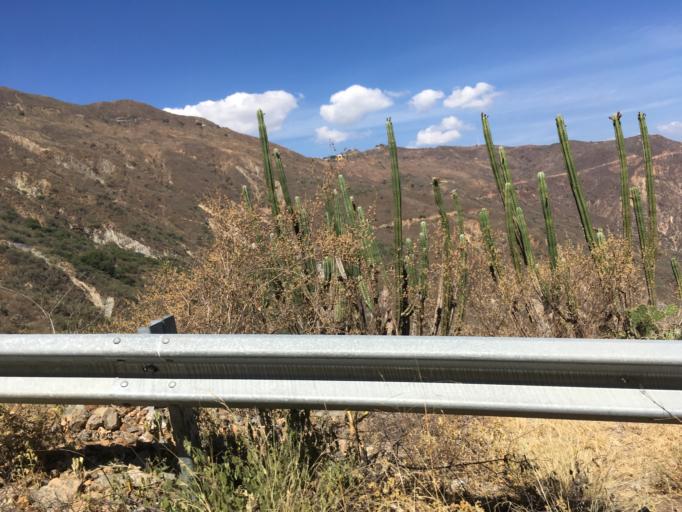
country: CO
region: Santander
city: Aratoca
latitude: 6.7710
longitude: -72.9890
